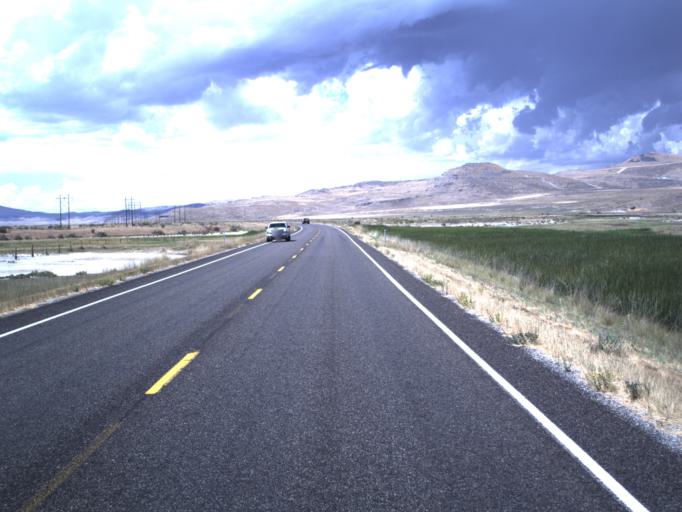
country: US
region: Utah
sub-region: Box Elder County
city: Tremonton
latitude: 41.6074
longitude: -112.3251
